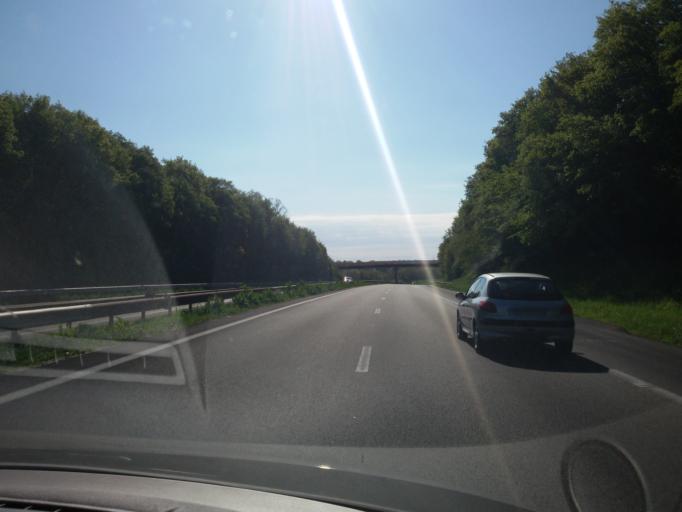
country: FR
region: Bourgogne
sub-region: Departement de l'Yonne
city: Vermenton
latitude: 47.7108
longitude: 3.7853
